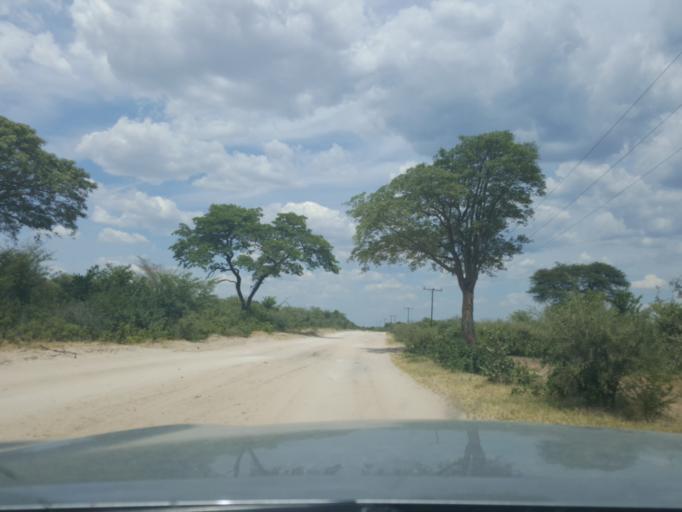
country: BW
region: North West
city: Shakawe
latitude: -18.4860
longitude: 22.1178
